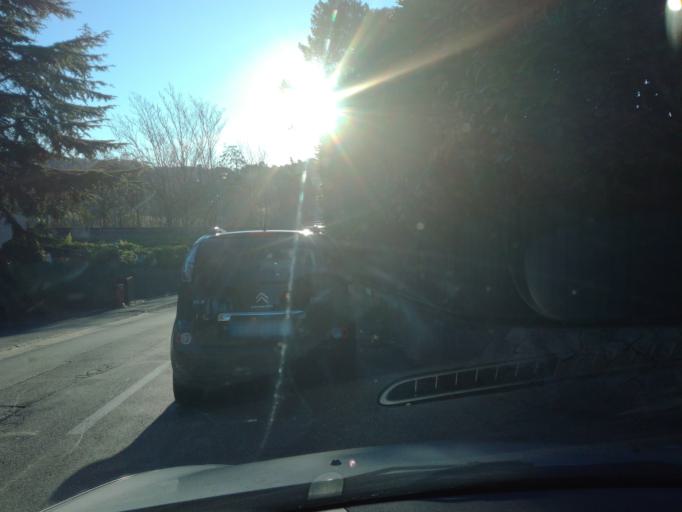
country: FR
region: Provence-Alpes-Cote d'Azur
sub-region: Departement des Alpes-Maritimes
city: La Roquette-sur-Siagne
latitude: 43.6071
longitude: 6.9703
